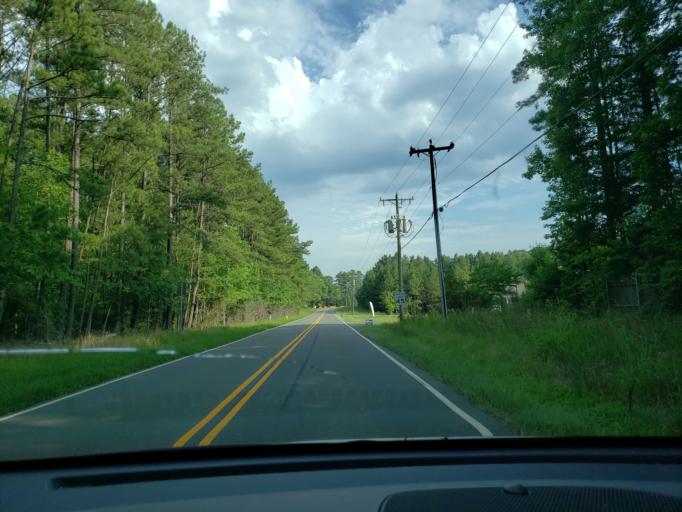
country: US
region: North Carolina
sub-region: Orange County
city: Chapel Hill
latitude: 35.9007
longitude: -78.9810
